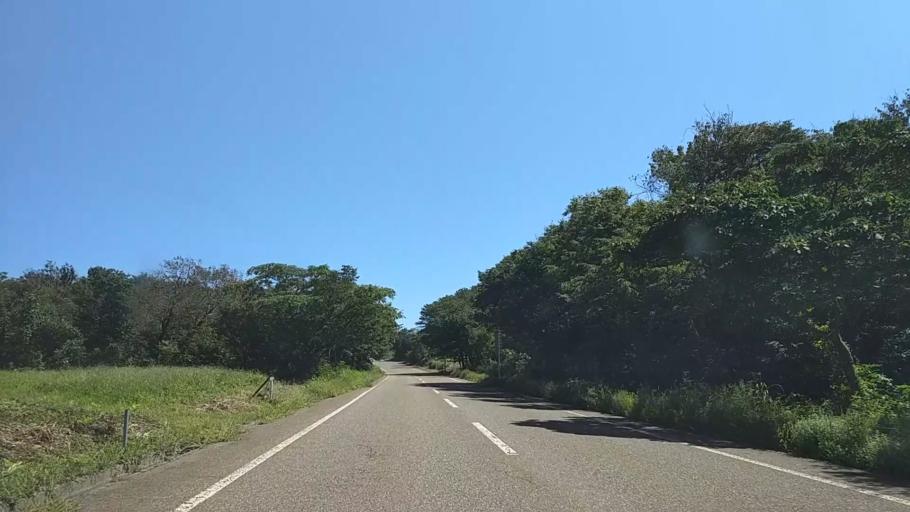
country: JP
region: Niigata
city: Joetsu
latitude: 37.1721
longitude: 138.1026
